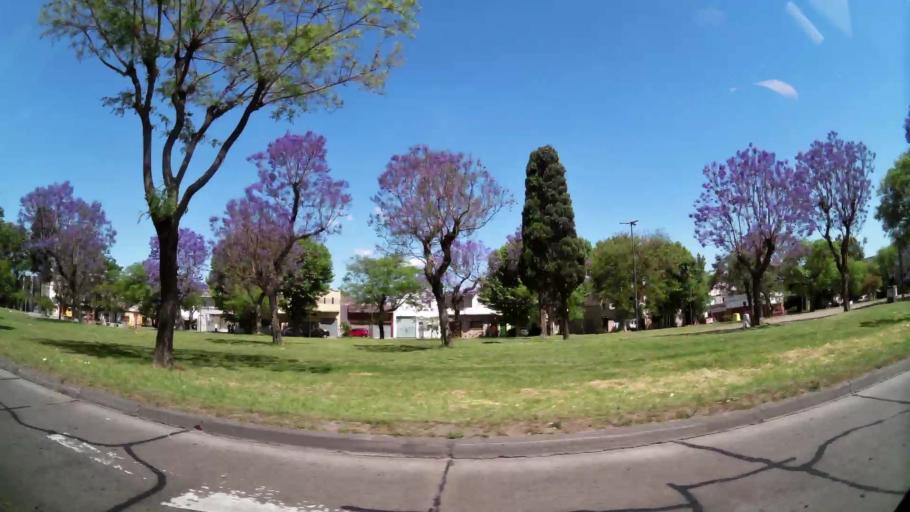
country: AR
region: Buenos Aires F.D.
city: Villa Lugano
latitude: -34.6590
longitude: -58.4274
